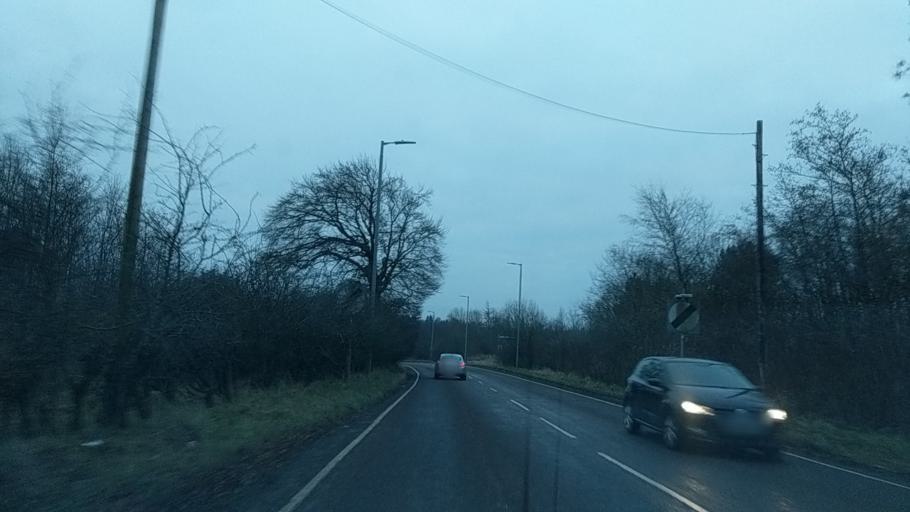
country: GB
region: Scotland
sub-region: South Lanarkshire
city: East Kilbride
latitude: 55.7417
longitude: -4.1577
